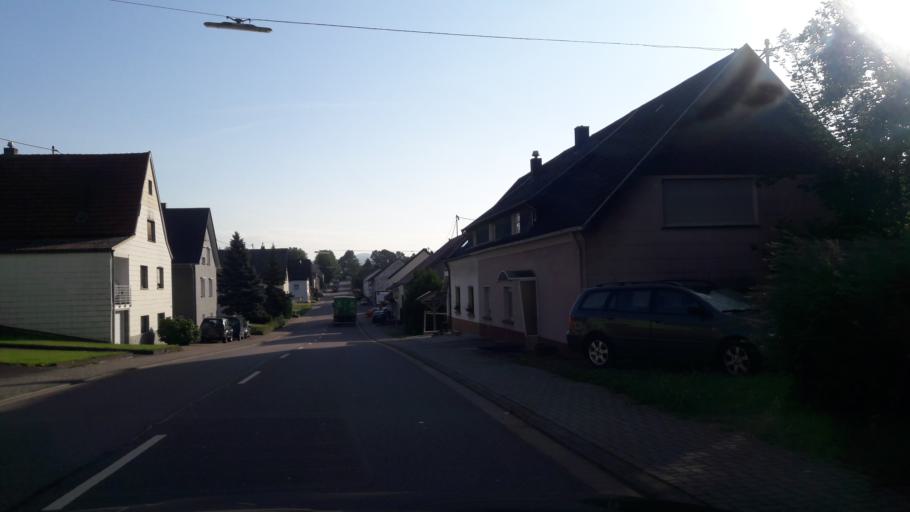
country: DE
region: Saarland
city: Eppelborn
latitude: 49.4373
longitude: 6.9554
